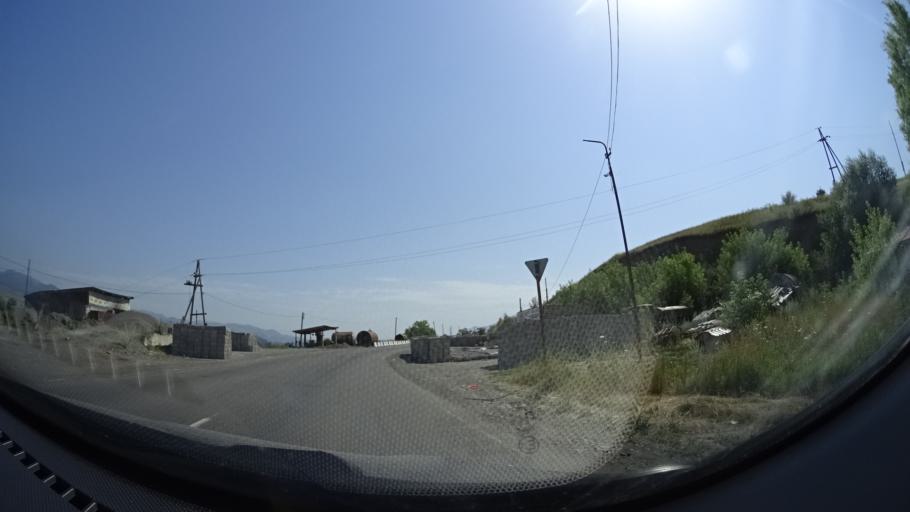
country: GE
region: Samtskhe-Javakheti
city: Akhaltsikhe
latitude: 41.6411
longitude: 43.0230
